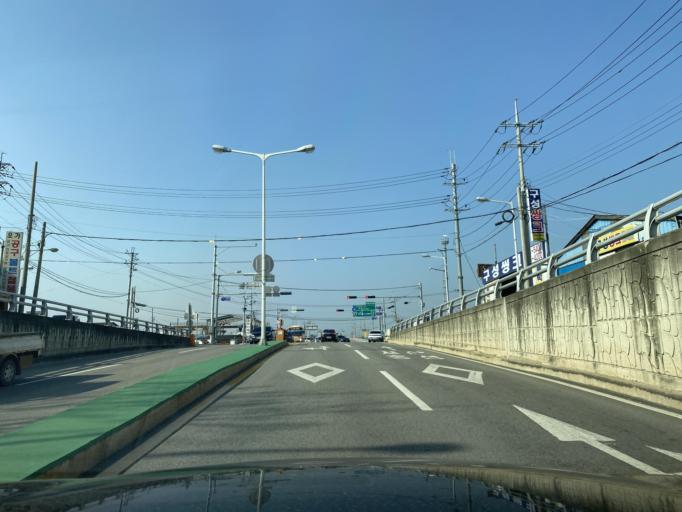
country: KR
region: Chungcheongnam-do
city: Yesan
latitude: 36.6828
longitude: 126.8275
